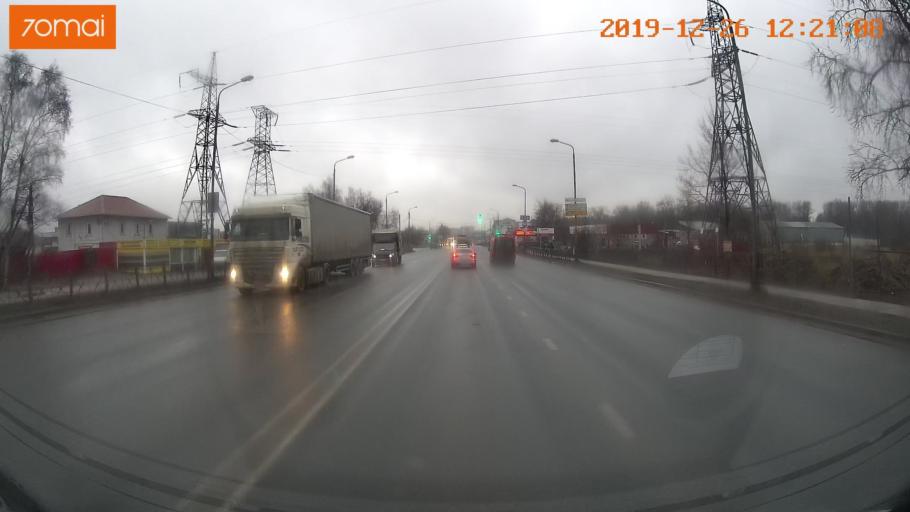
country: RU
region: Vologda
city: Cherepovets
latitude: 59.1533
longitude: 37.9312
